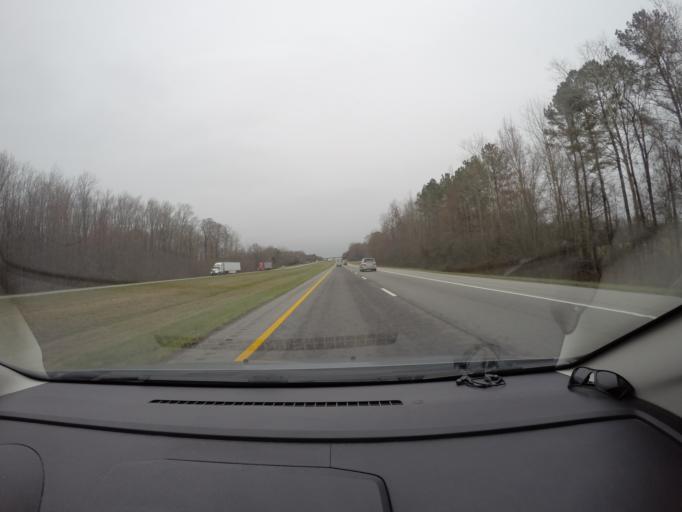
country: US
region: Tennessee
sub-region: Coffee County
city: Manchester
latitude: 35.4029
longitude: -86.0018
